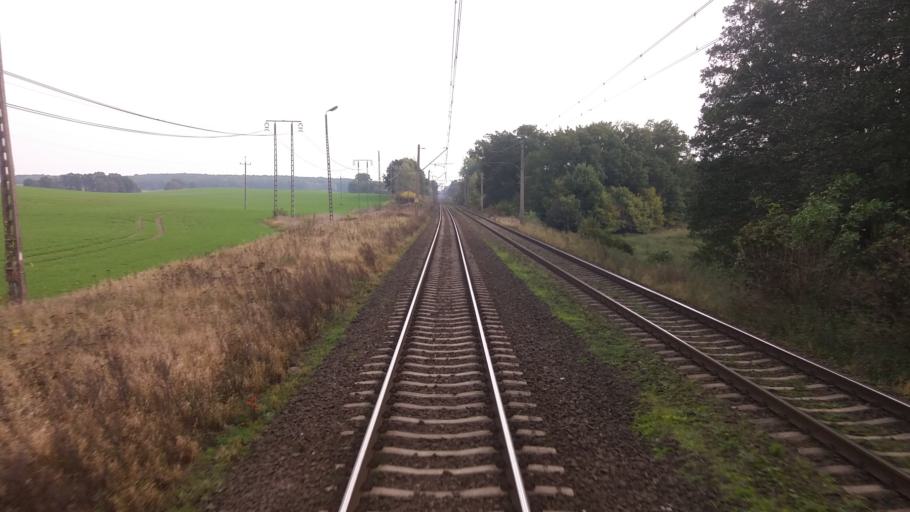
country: PL
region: West Pomeranian Voivodeship
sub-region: Powiat stargardzki
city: Dolice
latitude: 53.1949
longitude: 15.2250
